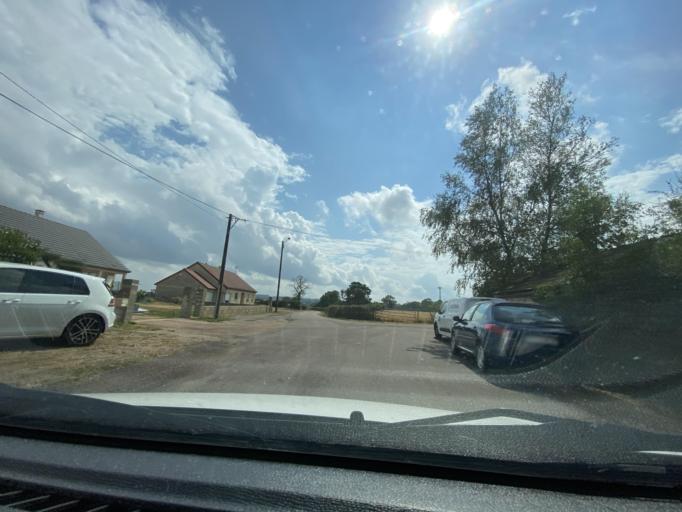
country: FR
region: Bourgogne
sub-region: Departement de la Cote-d'Or
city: Saulieu
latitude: 47.2994
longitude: 4.2368
